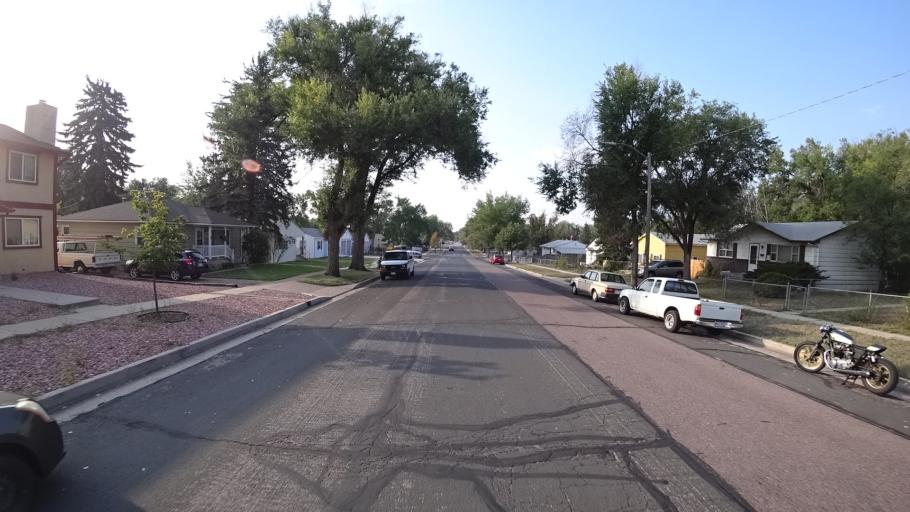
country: US
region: Colorado
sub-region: El Paso County
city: Colorado Springs
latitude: 38.8418
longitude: -104.7900
